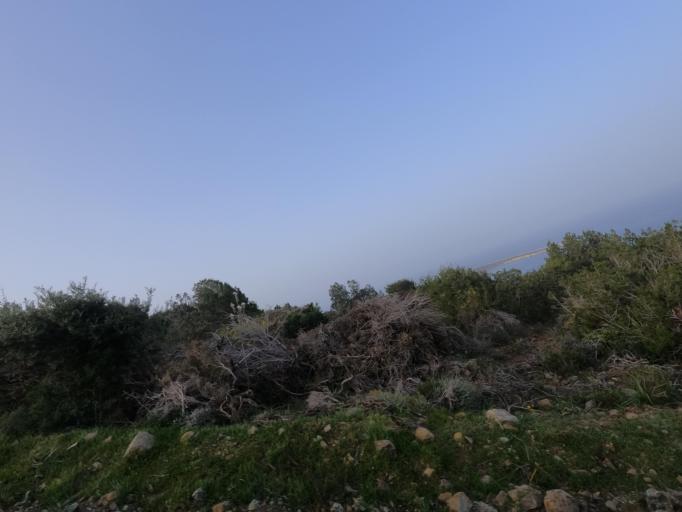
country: CY
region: Pafos
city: Pegeia
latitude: 34.9677
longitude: 32.3236
